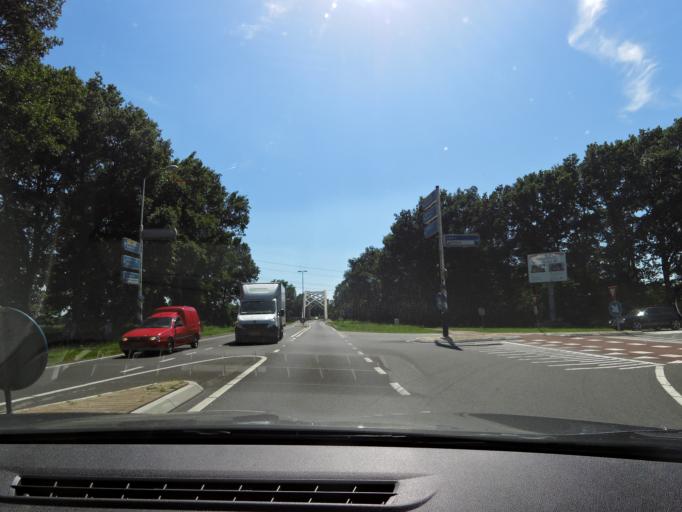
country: NL
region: Overijssel
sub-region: Gemeente Hof van Twente
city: Goor
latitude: 52.2287
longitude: 6.6034
